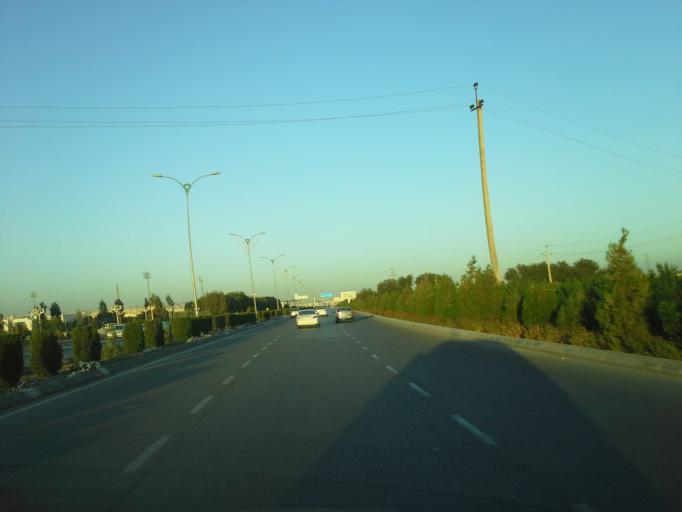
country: TM
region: Dasoguz
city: Dasoguz
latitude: 41.8235
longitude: 59.9277
